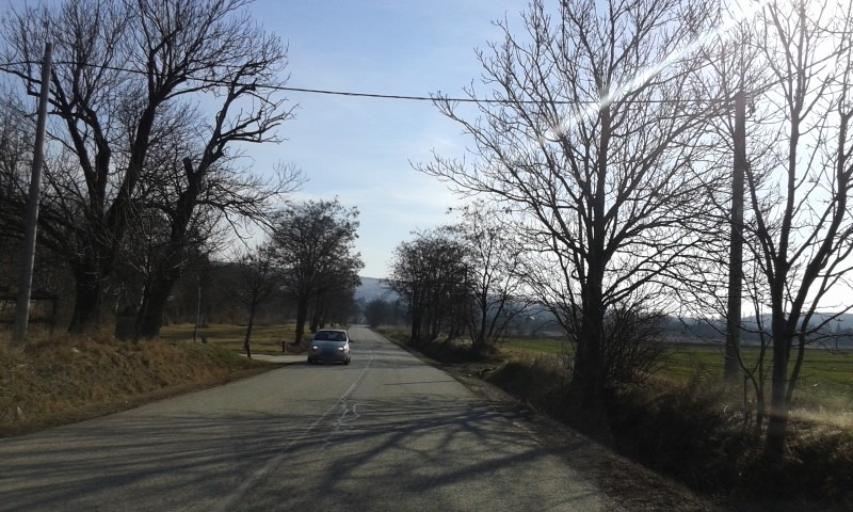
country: HU
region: Pest
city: Soskut
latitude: 47.4071
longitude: 18.8131
